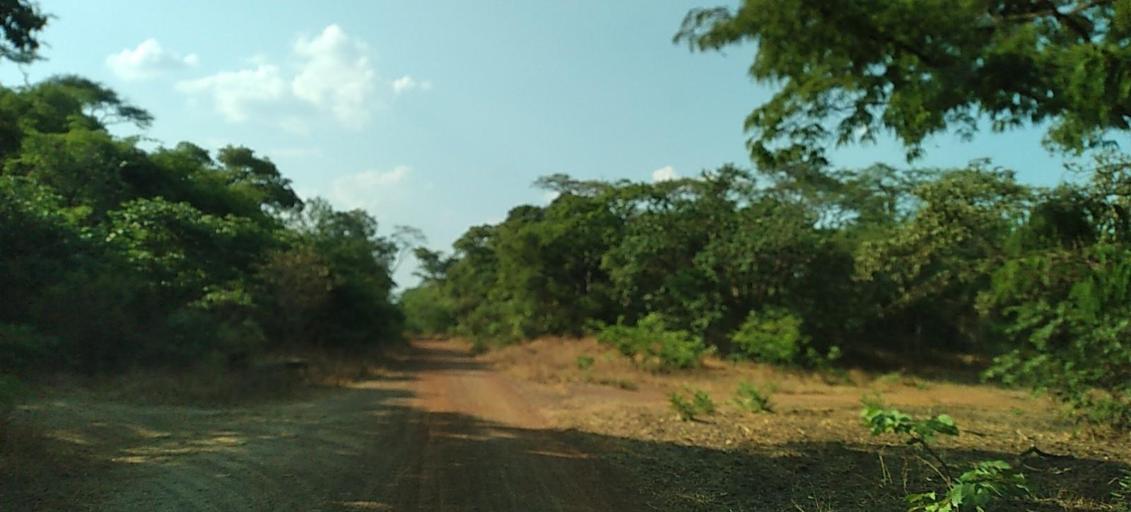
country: ZM
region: Copperbelt
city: Mpongwe
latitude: -13.4499
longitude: 28.0650
